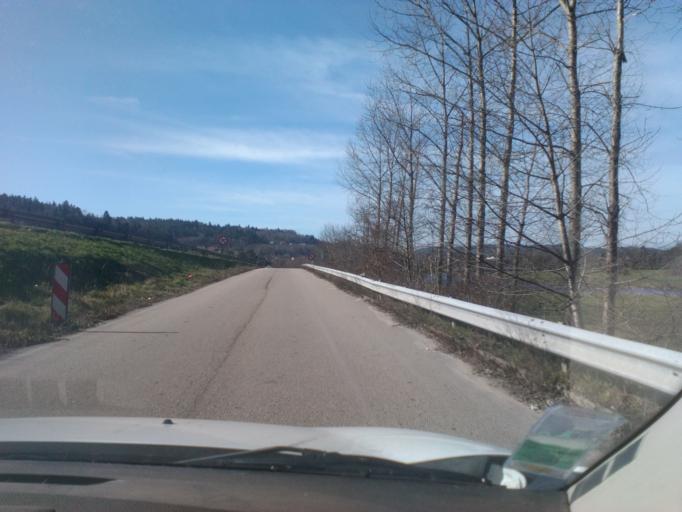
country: FR
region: Lorraine
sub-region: Departement des Vosges
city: Pouxeux
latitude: 48.1104
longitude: 6.5726
